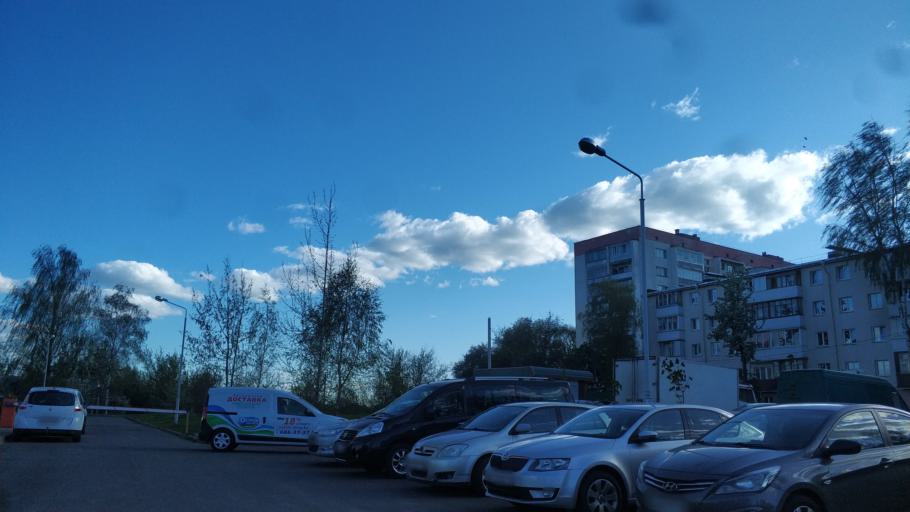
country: BY
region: Minsk
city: Minsk
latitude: 53.8712
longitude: 27.5800
